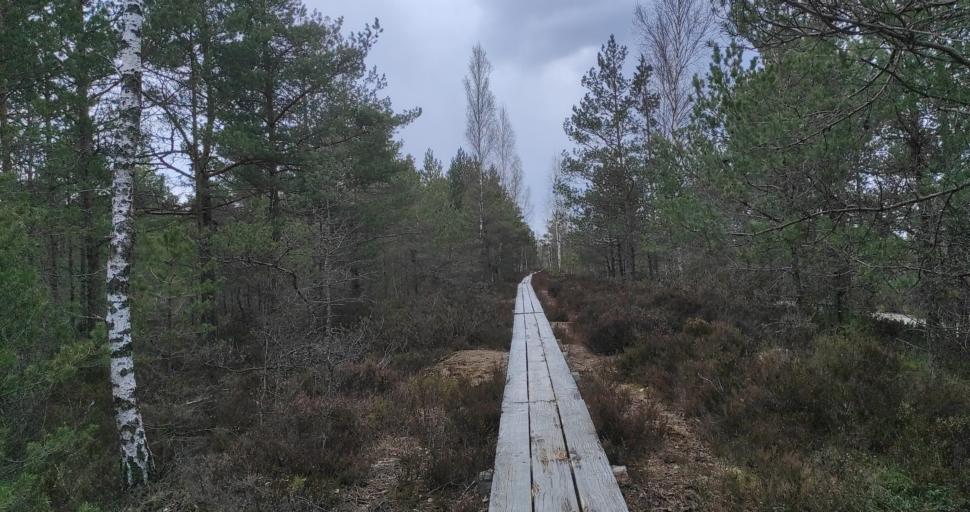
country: LV
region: Dundaga
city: Dundaga
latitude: 57.3490
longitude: 22.1500
